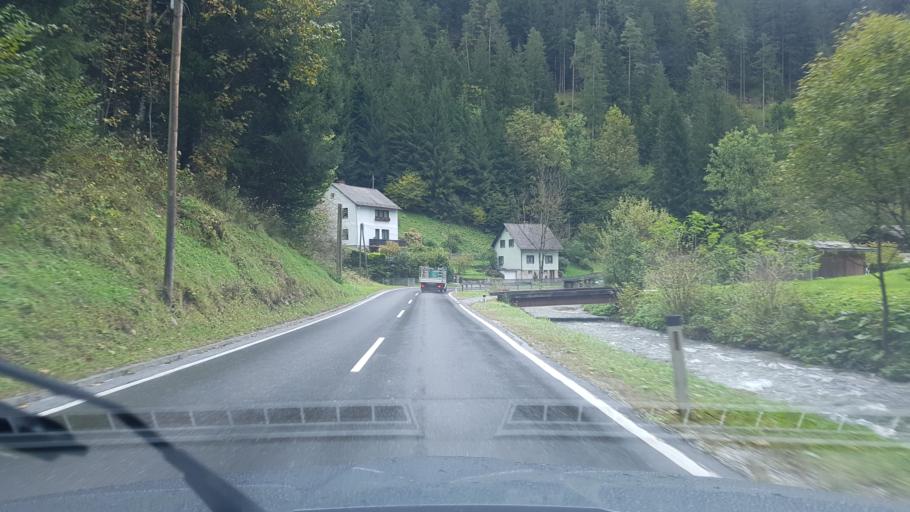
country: AT
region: Styria
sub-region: Politischer Bezirk Voitsberg
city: Salla
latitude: 47.1130
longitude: 15.0085
